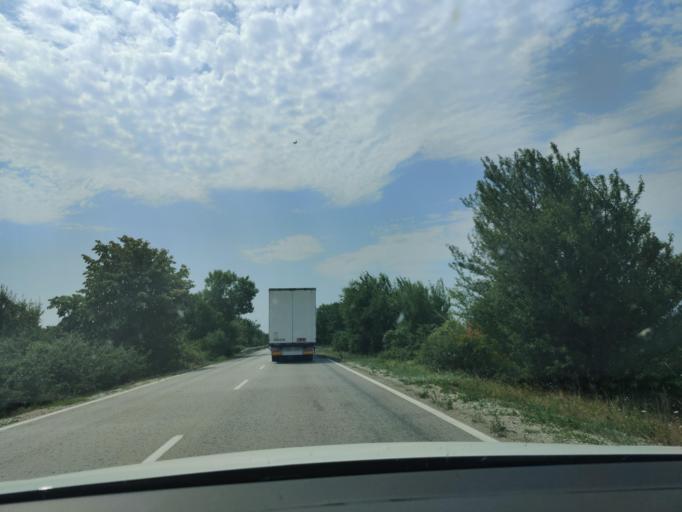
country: BG
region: Vidin
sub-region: Obshtina Vidin
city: Dunavtsi
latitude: 43.8613
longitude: 22.7819
